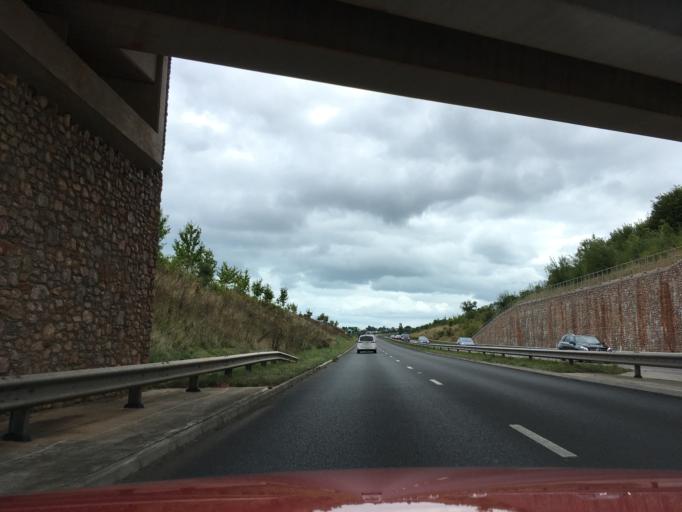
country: GB
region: England
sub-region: Devon
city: Kingskerswell
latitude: 50.4949
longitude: -3.5851
